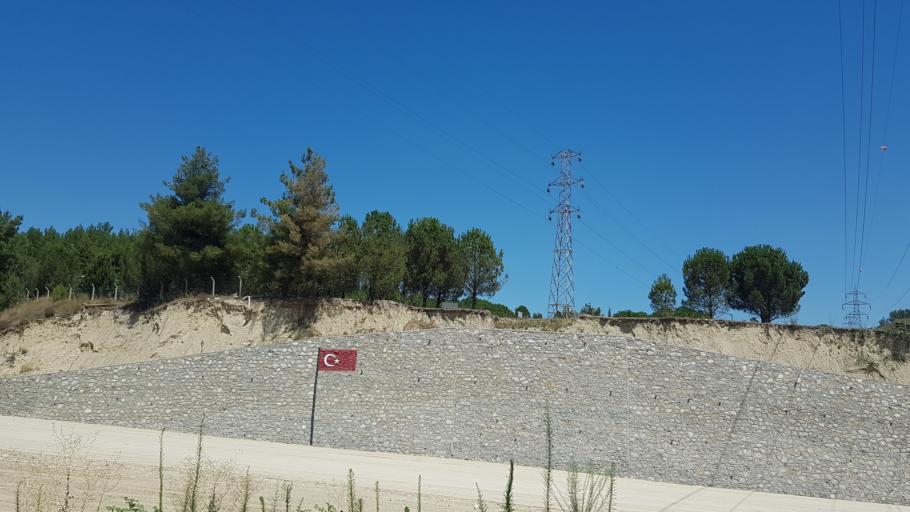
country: TR
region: Mugla
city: Yatagan
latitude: 37.3182
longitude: 28.0832
